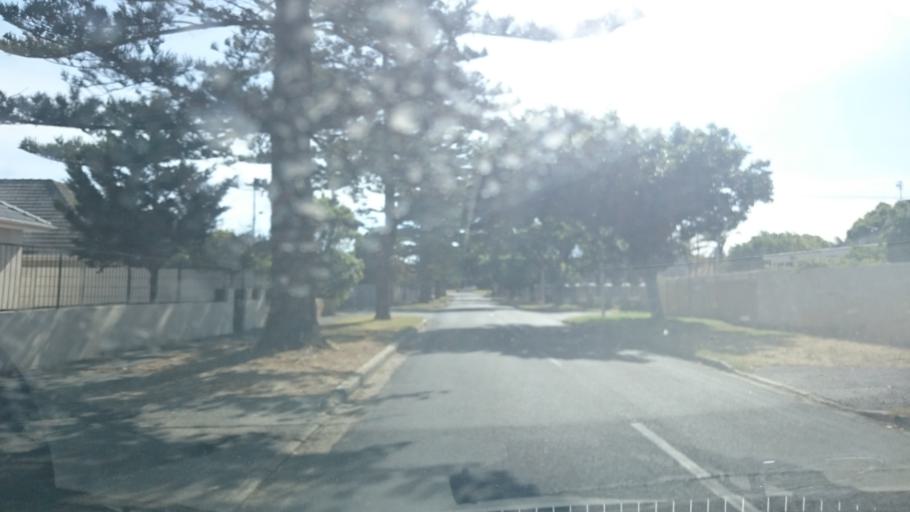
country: ZA
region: Western Cape
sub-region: City of Cape Town
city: Lansdowne
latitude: -34.0175
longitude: 18.4827
